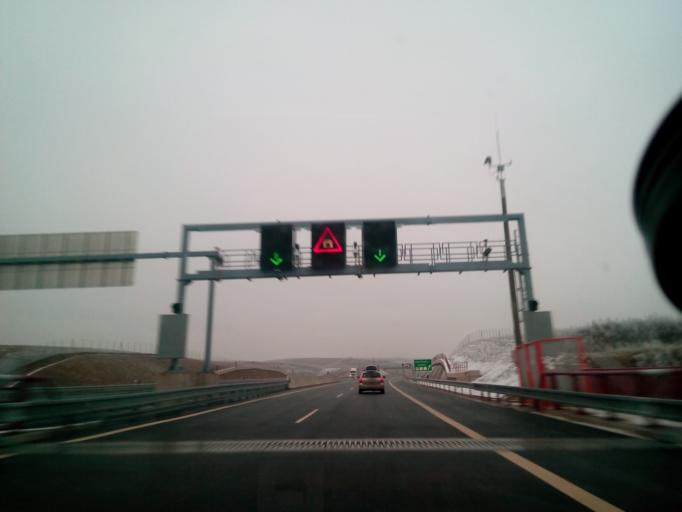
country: SK
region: Presovsky
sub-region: Okres Presov
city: Levoca
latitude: 49.0084
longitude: 20.5962
